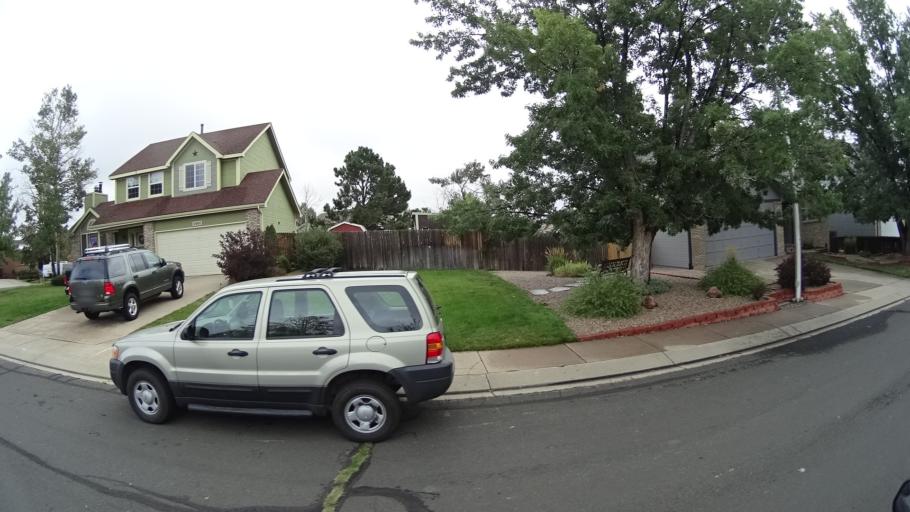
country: US
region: Colorado
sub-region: El Paso County
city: Cimarron Hills
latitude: 38.9228
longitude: -104.7532
